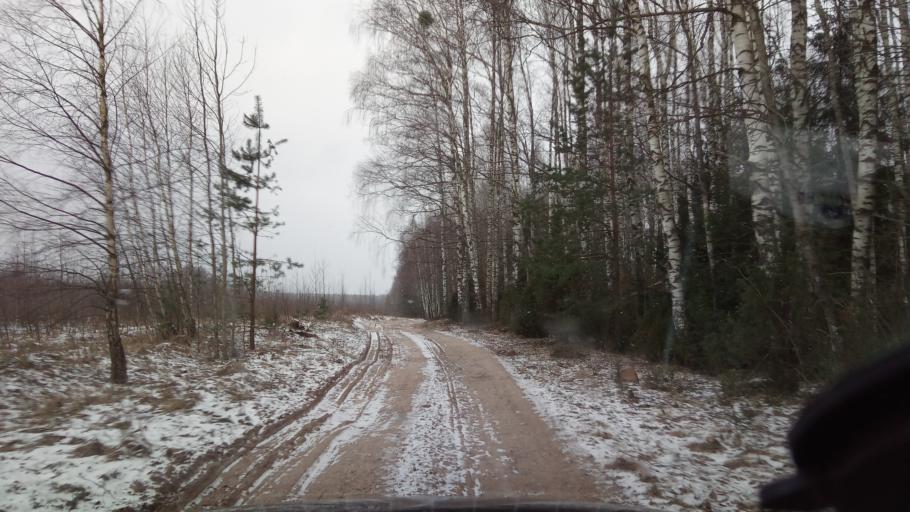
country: LT
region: Alytaus apskritis
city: Varena
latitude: 54.1333
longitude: 24.7017
